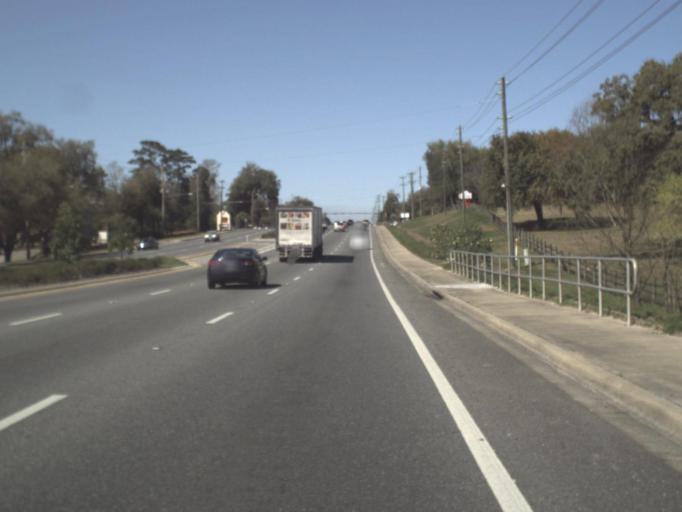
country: US
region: Florida
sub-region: Leon County
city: Tallahassee
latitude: 30.4372
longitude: -84.2265
